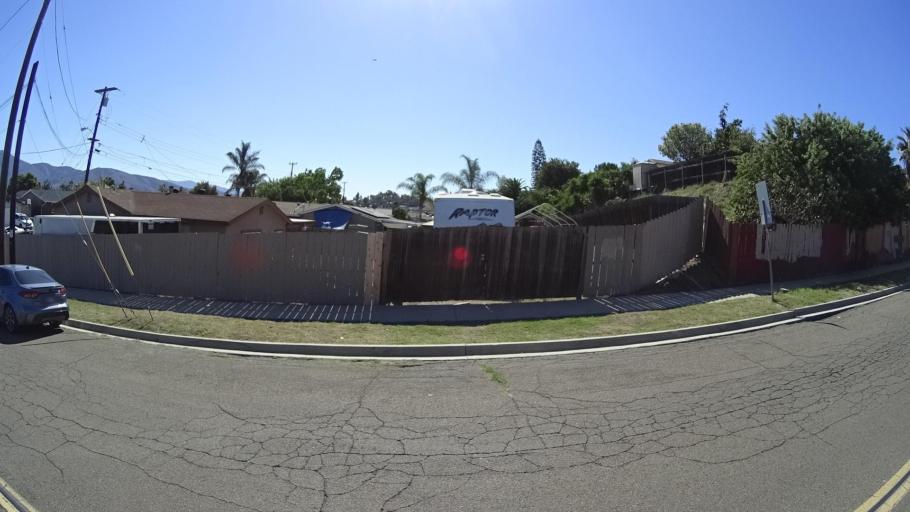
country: US
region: California
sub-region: San Diego County
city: La Presa
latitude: 32.7081
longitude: -117.0200
